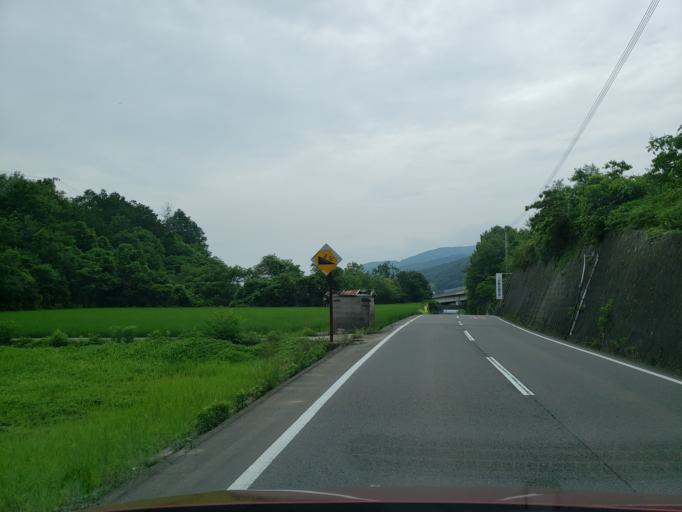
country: JP
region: Tokushima
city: Wakimachi
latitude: 34.1042
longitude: 134.2423
